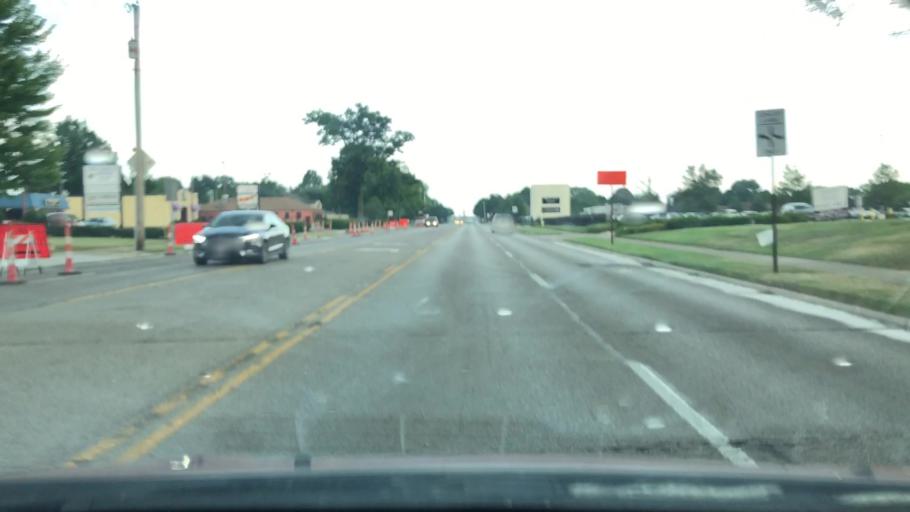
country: US
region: Ohio
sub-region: Montgomery County
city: Centerville
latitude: 39.6606
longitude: -84.1268
